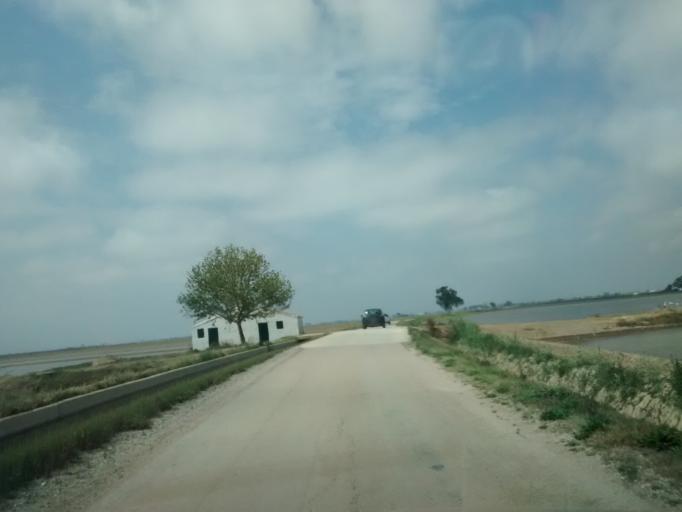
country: ES
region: Catalonia
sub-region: Provincia de Tarragona
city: Deltebre
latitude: 40.6842
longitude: 0.7892
